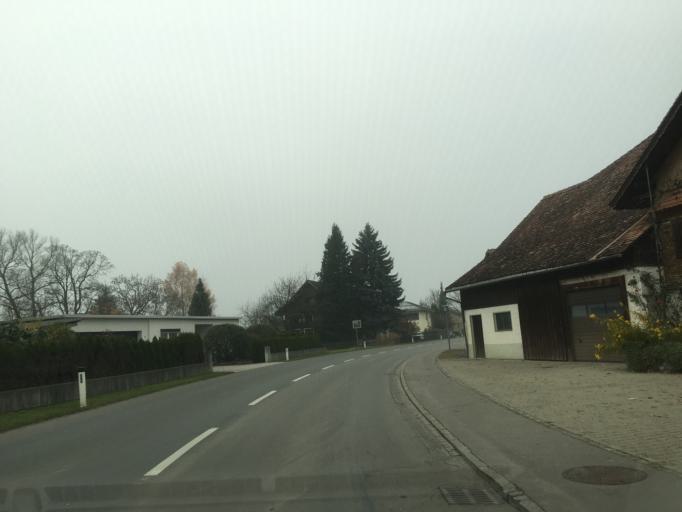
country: AT
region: Vorarlberg
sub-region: Politischer Bezirk Feldkirch
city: Koblach
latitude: 47.3180
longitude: 9.5989
